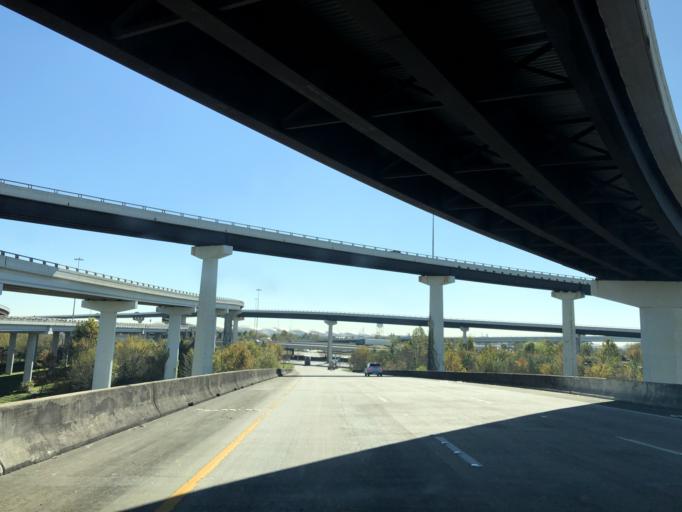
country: US
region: Texas
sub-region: Harris County
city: Cloverleaf
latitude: 29.7735
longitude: -95.1567
